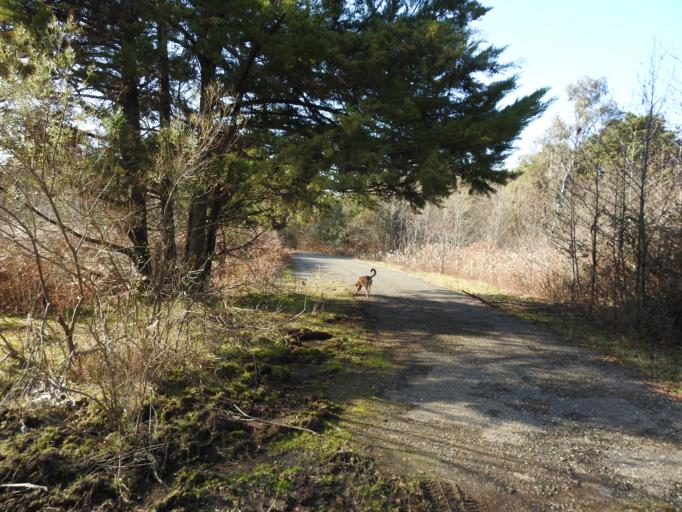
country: GE
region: Abkhazia
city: Dranda
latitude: 42.7949
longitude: 41.2596
